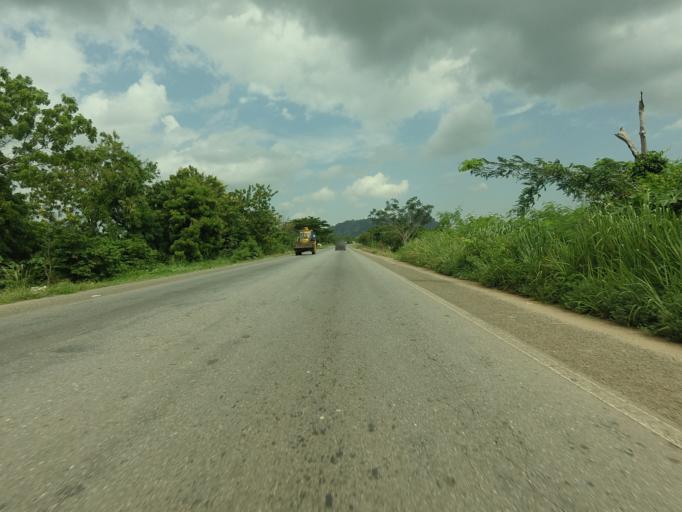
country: GH
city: Akropong
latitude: 6.1164
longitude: 0.0492
